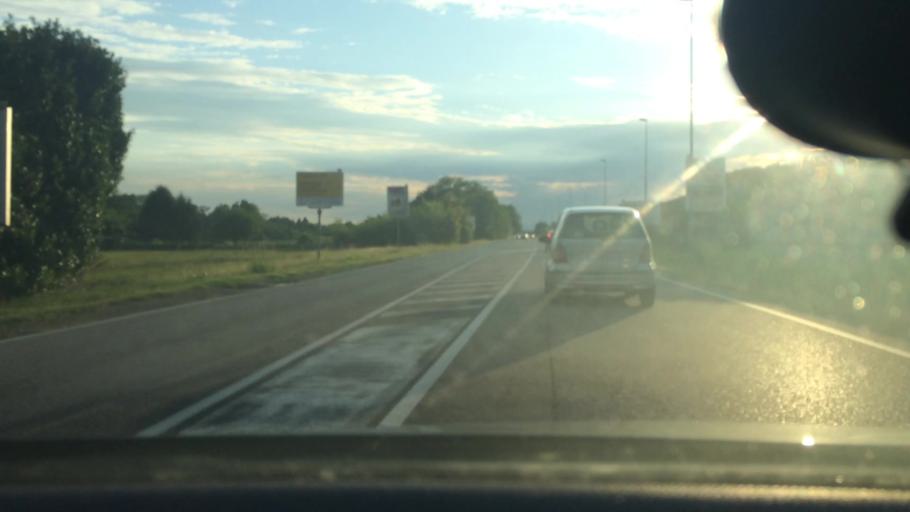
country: IT
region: Lombardy
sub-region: Citta metropolitana di Milano
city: Parabiago
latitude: 45.5476
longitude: 8.9379
